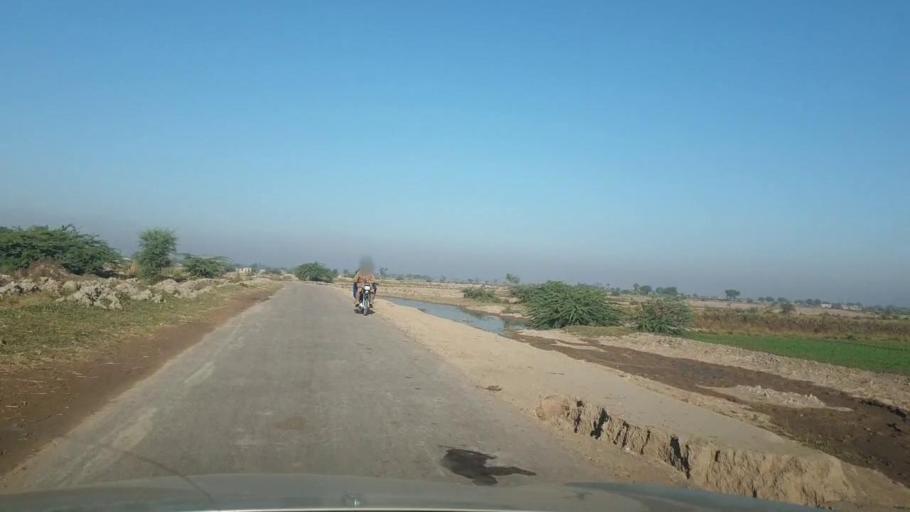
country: PK
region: Sindh
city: Bhan
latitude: 26.5521
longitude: 67.6968
